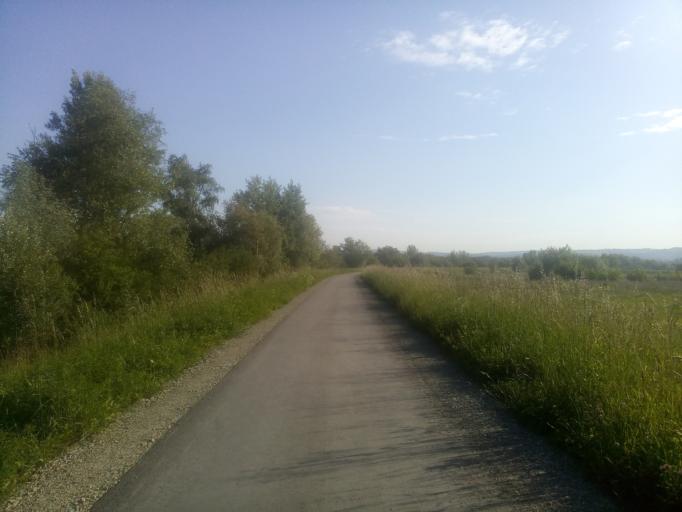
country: PL
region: Lesser Poland Voivodeship
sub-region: Powiat nowosadecki
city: Chelmiec
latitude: 49.6052
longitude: 20.6717
